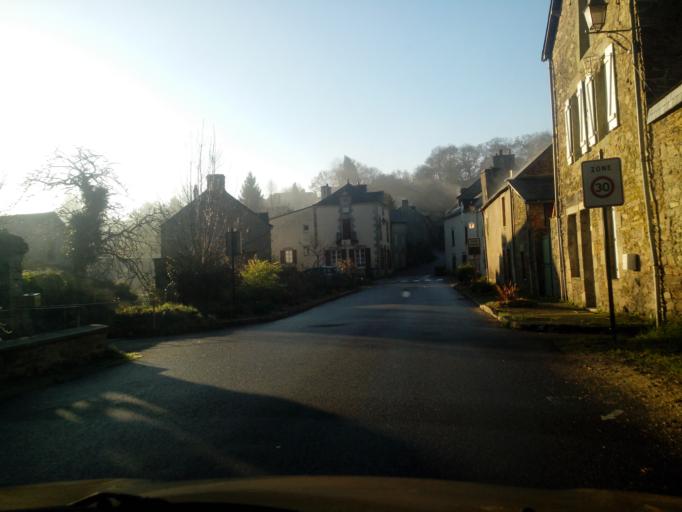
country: FR
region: Brittany
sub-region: Departement du Morbihan
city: Pluherlin
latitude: 47.7024
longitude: -2.3376
